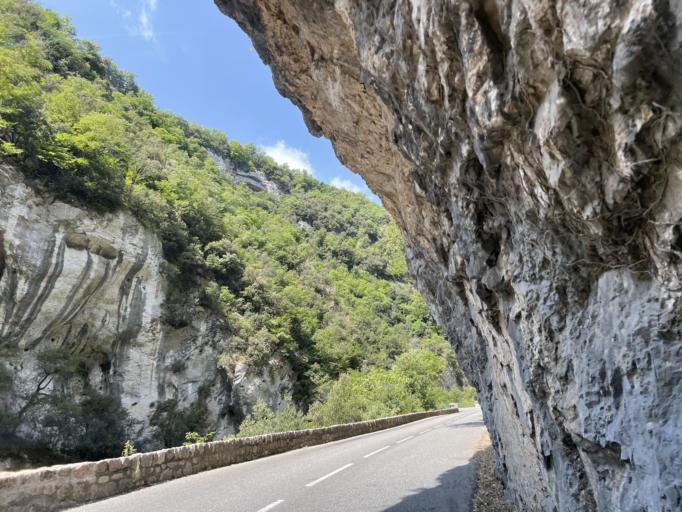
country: FR
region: Provence-Alpes-Cote d'Azur
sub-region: Departement des Alpes-Maritimes
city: Tourrettes-sur-Loup
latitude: 43.7420
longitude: 7.0001
